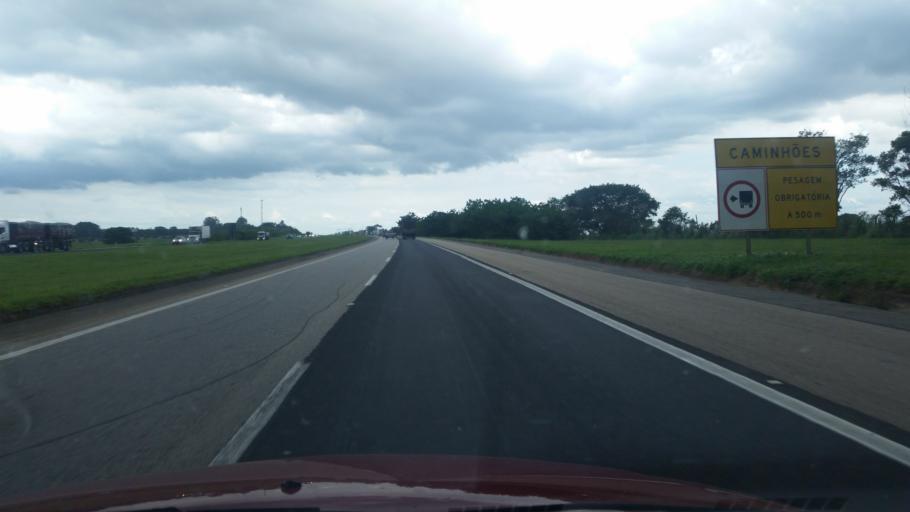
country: BR
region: Sao Paulo
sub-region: Porto Feliz
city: Porto Feliz
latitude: -23.3554
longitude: -47.5063
